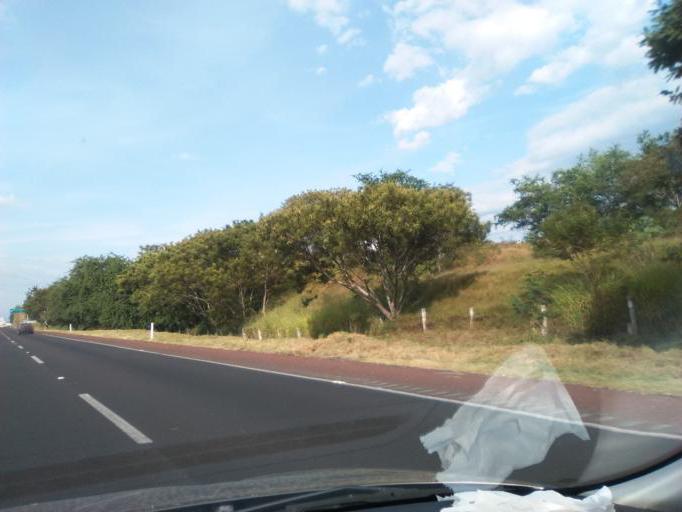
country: MX
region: Morelos
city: Alpuyeca
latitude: 18.7296
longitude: -99.2547
